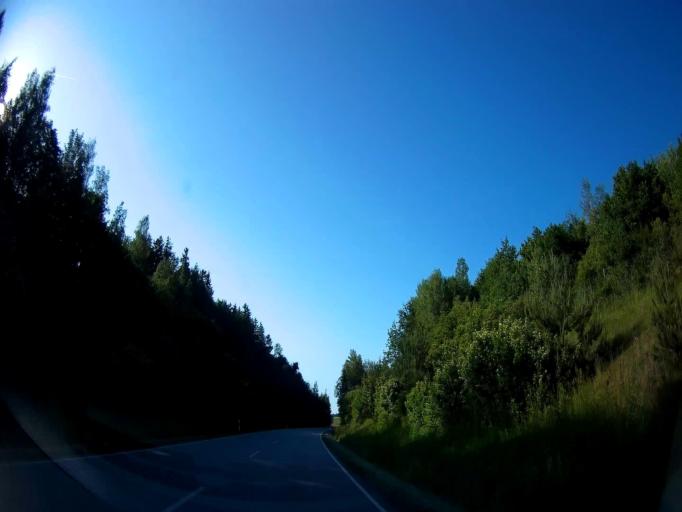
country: DE
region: Bavaria
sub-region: Lower Bavaria
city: Falkenberg
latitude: 48.4560
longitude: 12.7243
